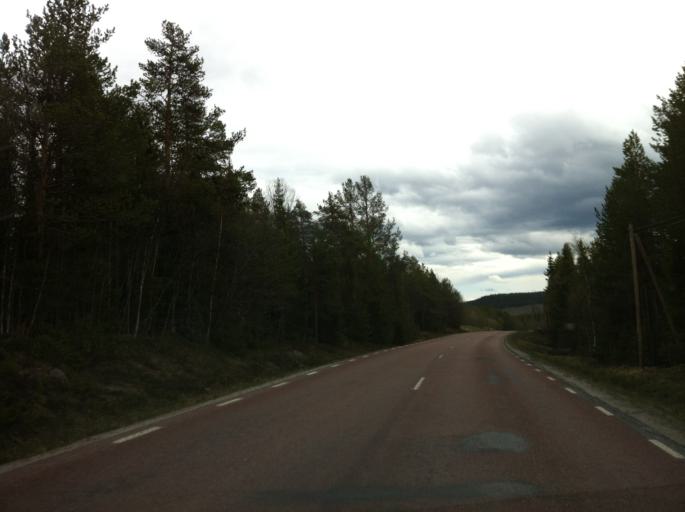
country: SE
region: Jaemtland
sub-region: Are Kommun
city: Are
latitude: 62.5941
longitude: 12.5440
